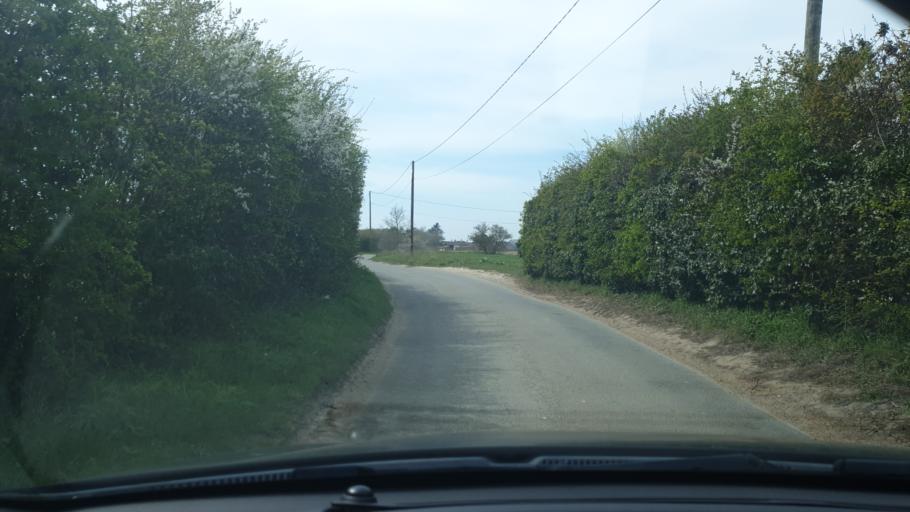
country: GB
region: England
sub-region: Essex
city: Little Clacton
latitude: 51.8991
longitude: 1.1685
